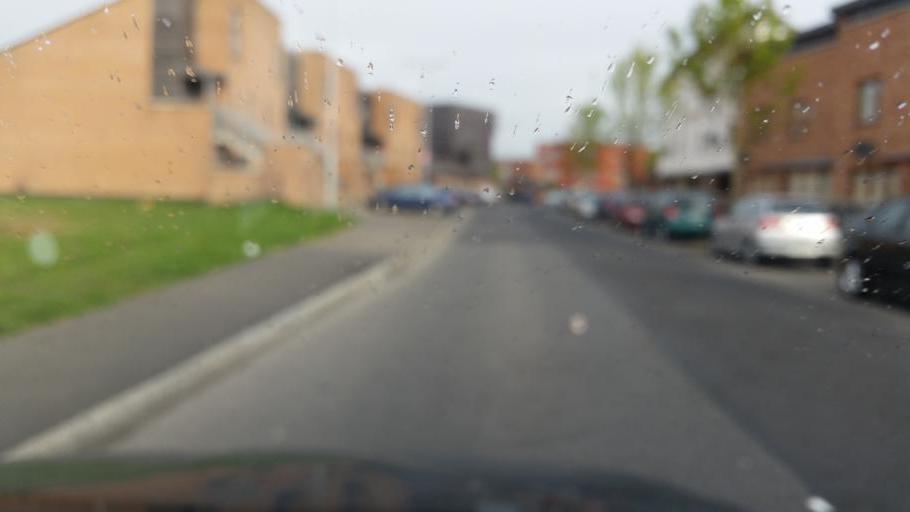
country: IE
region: Leinster
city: Ballymun
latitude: 53.3962
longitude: -6.2744
